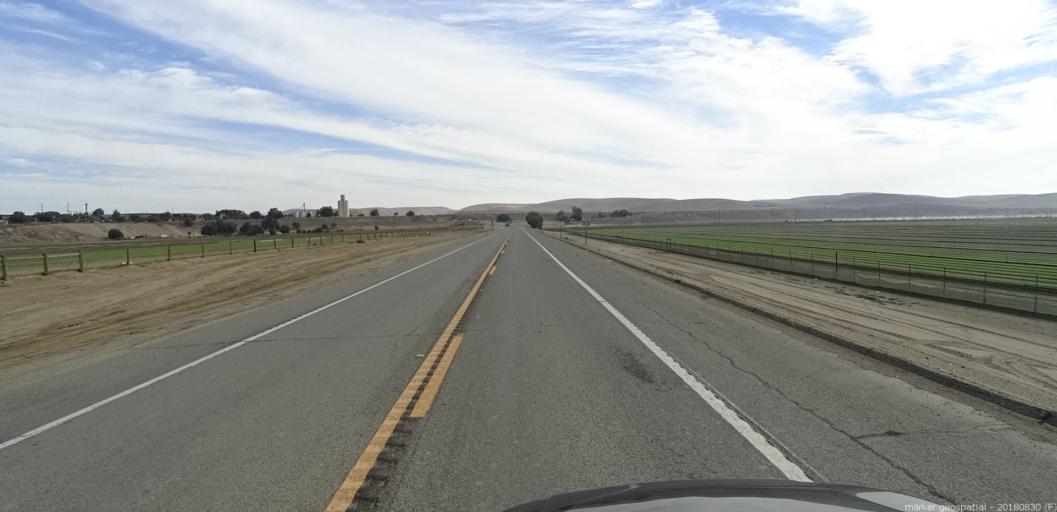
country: US
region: California
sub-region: Monterey County
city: King City
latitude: 36.1229
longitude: -121.0218
